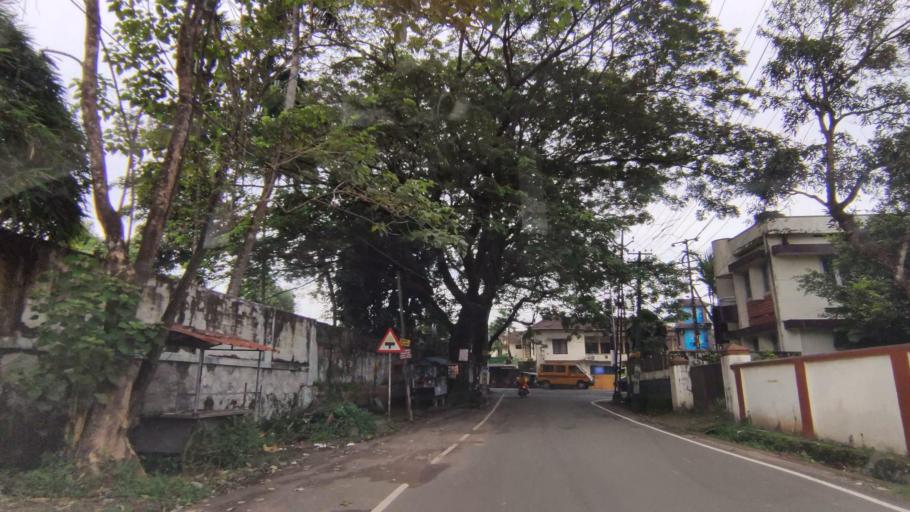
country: IN
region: Kerala
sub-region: Kottayam
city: Kottayam
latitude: 9.5957
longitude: 76.5121
